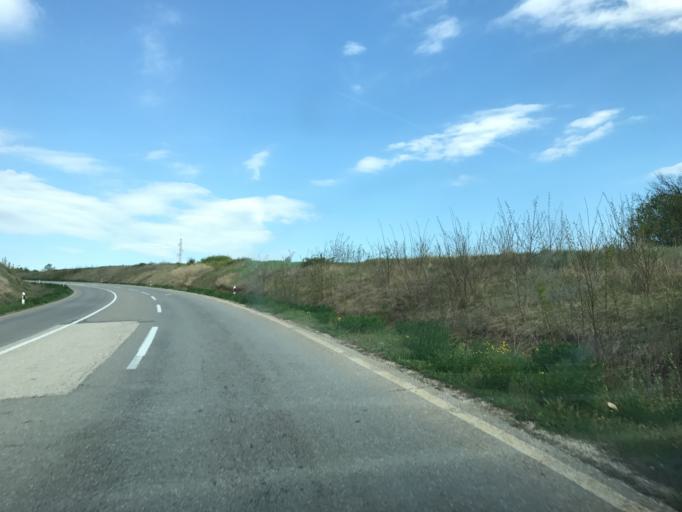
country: RS
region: Central Serbia
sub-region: Zajecarski Okrug
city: Zajecar
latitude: 44.0304
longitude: 22.3392
